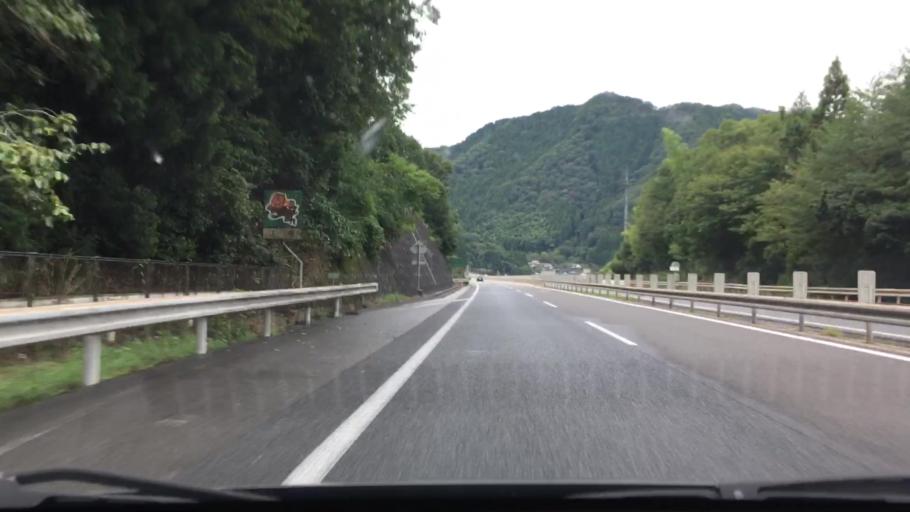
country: JP
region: Hiroshima
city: Hiroshima-shi
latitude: 34.5324
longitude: 132.4388
